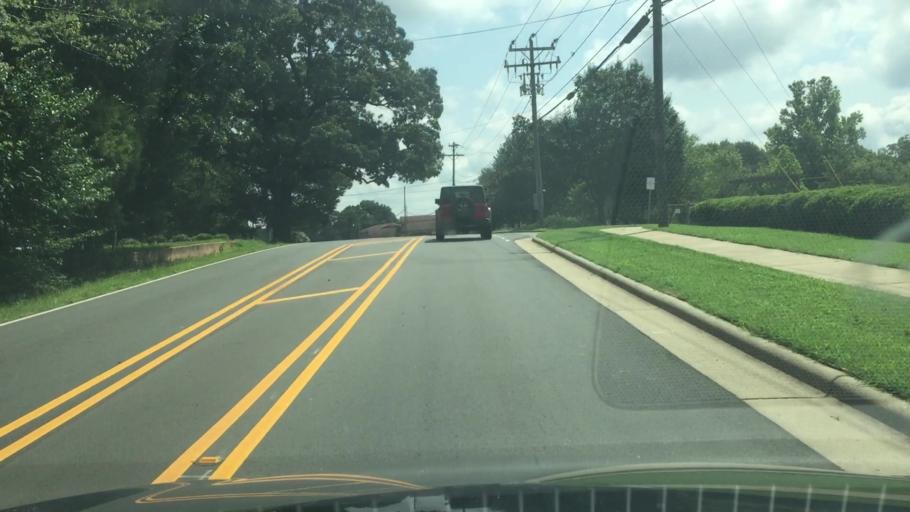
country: US
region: North Carolina
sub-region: Cabarrus County
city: Kannapolis
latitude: 35.4747
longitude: -80.6412
